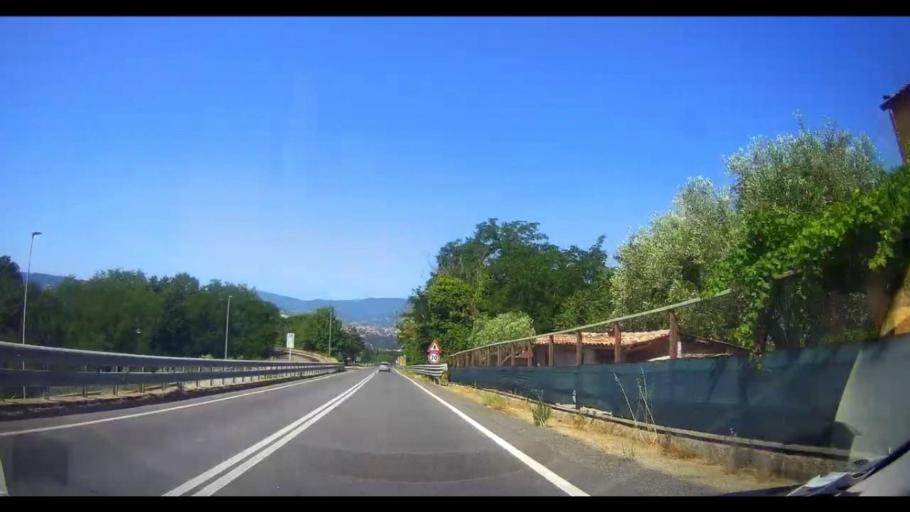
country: IT
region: Calabria
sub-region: Provincia di Cosenza
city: Zumpano
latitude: 39.2955
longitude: 16.2773
